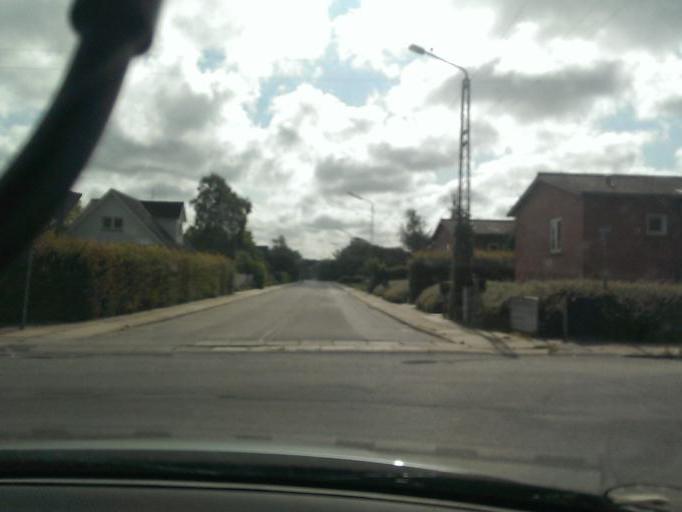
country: DK
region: North Denmark
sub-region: Hjorring Kommune
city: Vra
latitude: 57.3506
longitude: 9.9455
